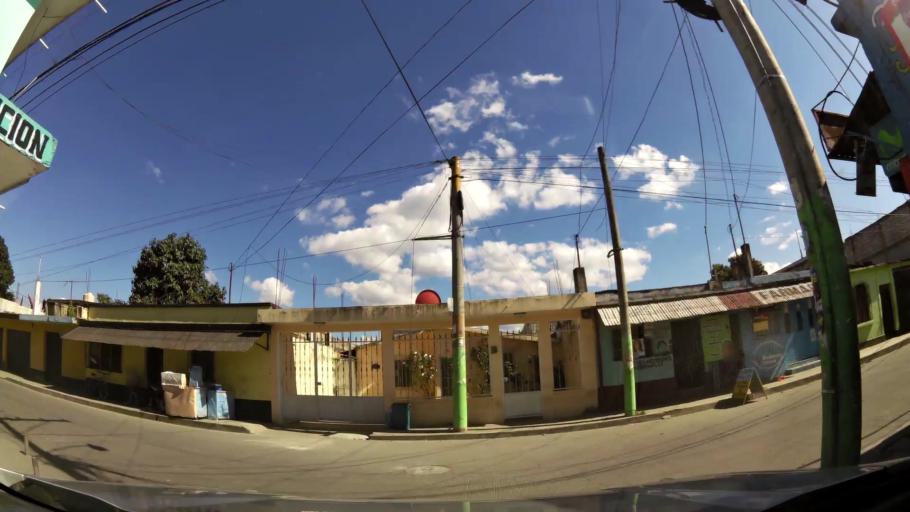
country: GT
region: Guatemala
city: Petapa
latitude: 14.5016
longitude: -90.5681
